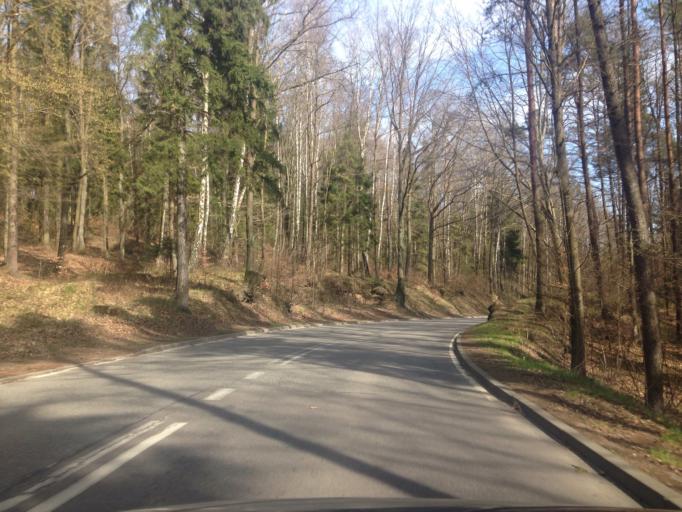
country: PL
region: Pomeranian Voivodeship
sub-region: Gdynia
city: Wielki Kack
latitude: 54.4770
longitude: 18.4549
